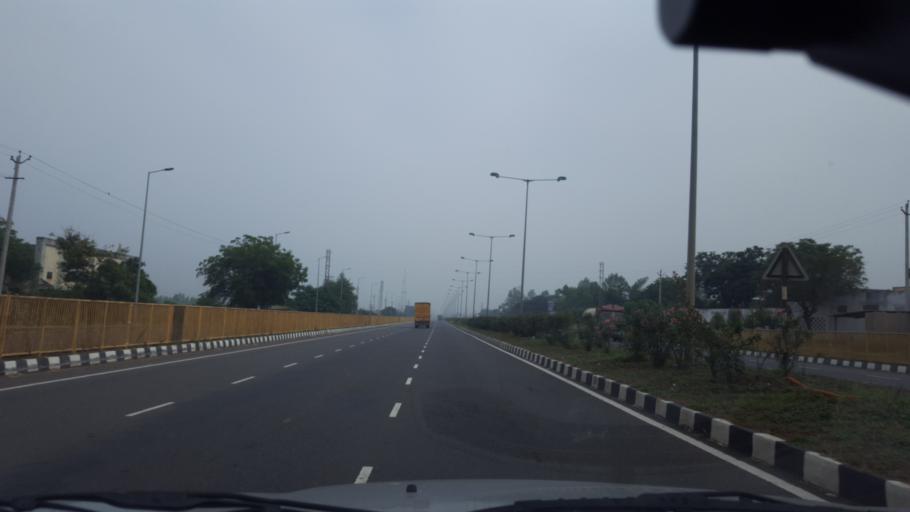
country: IN
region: Andhra Pradesh
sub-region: Prakasam
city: pedda nakkalapalem
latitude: 15.9662
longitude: 80.0935
